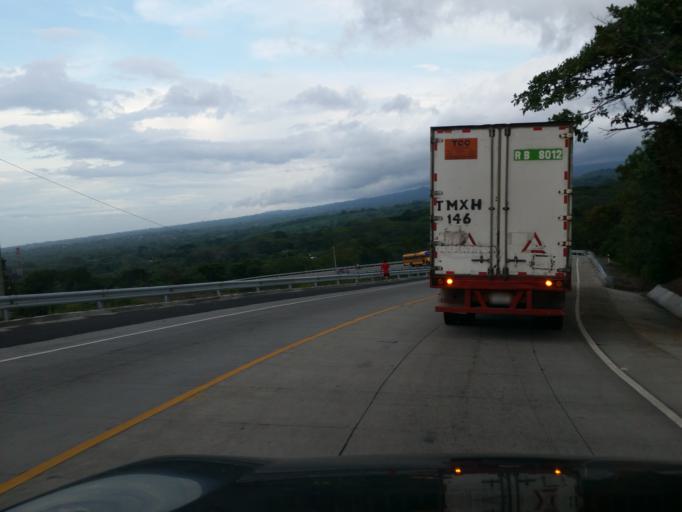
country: NI
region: Managua
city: Ciudad Sandino
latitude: 12.0806
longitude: -86.3731
